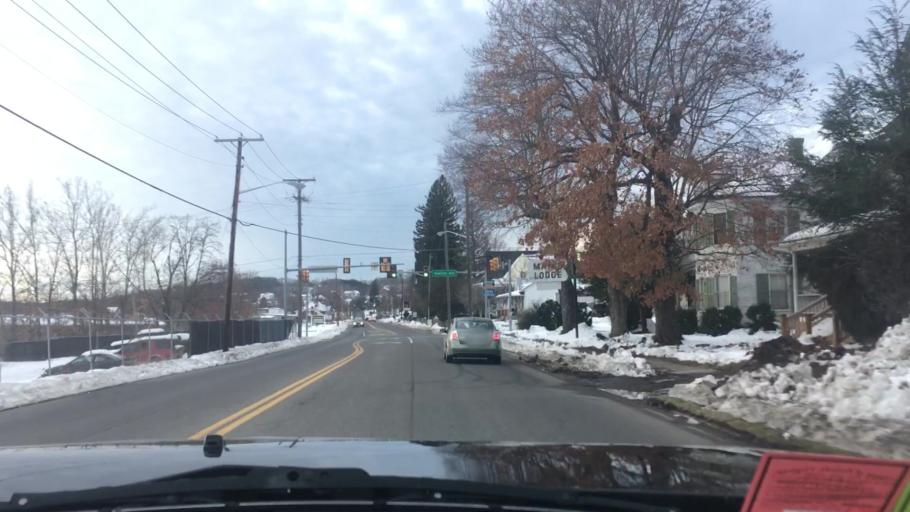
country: US
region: Virginia
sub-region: Pulaski County
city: Pulaski
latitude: 37.0513
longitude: -80.7765
